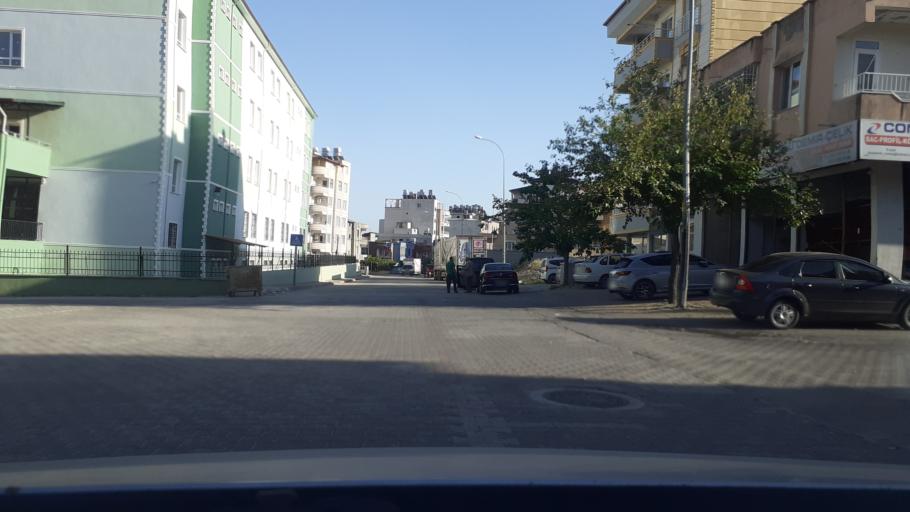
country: TR
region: Hatay
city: Kirikhan
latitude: 36.4983
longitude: 36.3653
